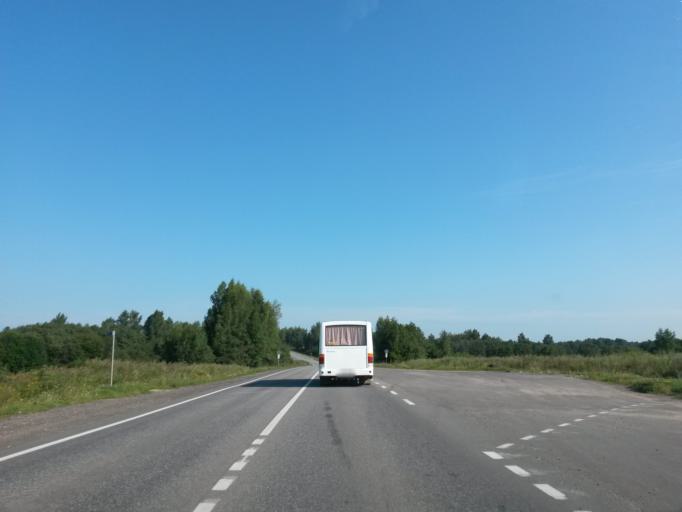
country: RU
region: Jaroslavl
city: Gavrilov-Yam
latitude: 57.3327
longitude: 39.9209
